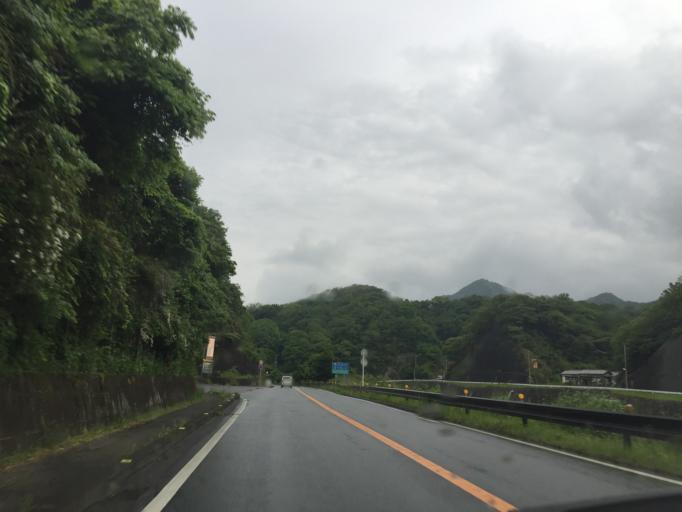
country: JP
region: Shizuoka
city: Mishima
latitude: 35.0477
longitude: 138.9126
